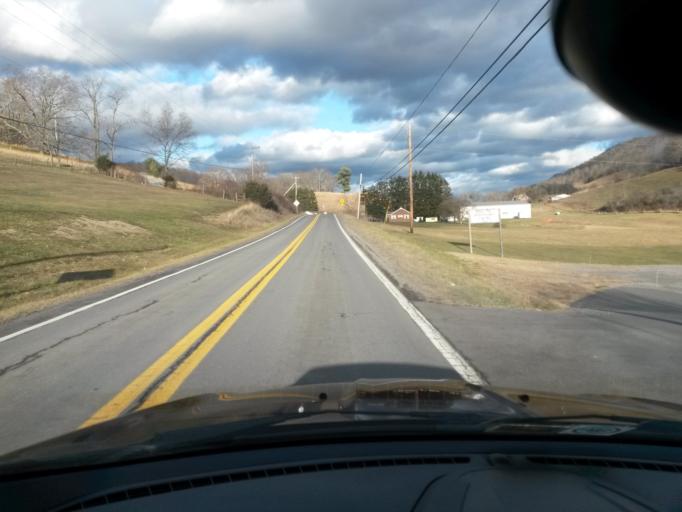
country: US
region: Virginia
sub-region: Giles County
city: Pembroke
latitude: 37.4551
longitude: -80.6683
